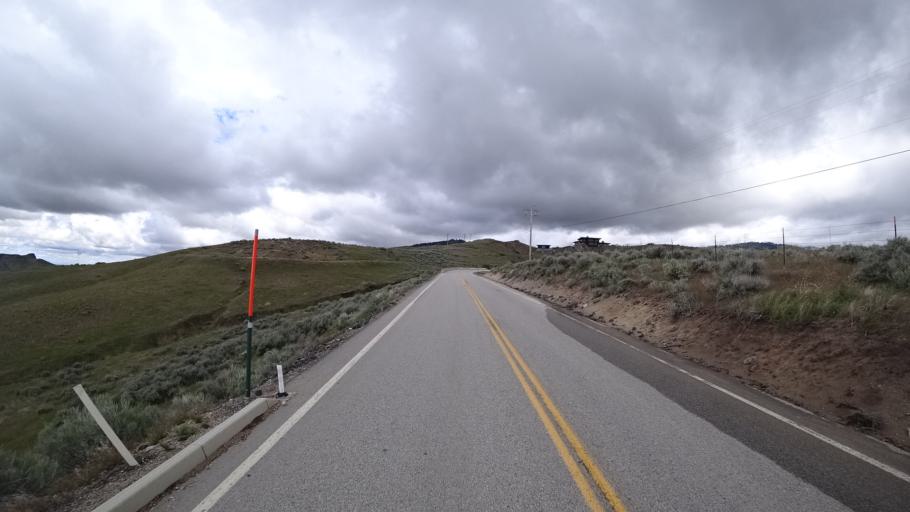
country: US
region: Idaho
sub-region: Ada County
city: Boise
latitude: 43.7094
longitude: -116.1643
